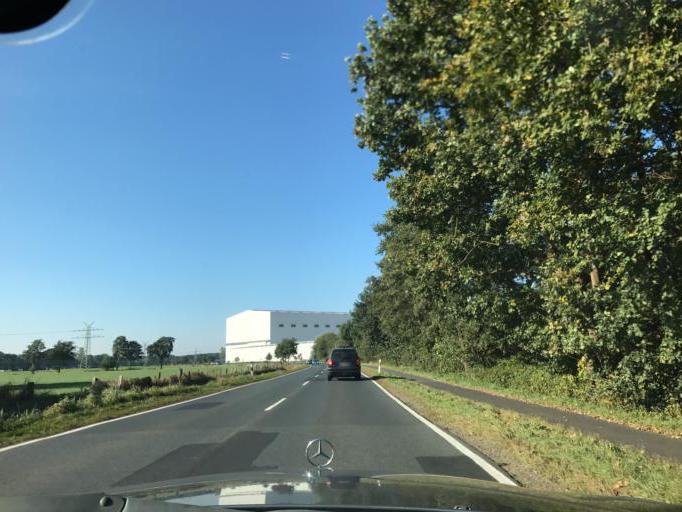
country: DE
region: Lower Saxony
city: Papenburg
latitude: 53.0910
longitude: 7.3689
